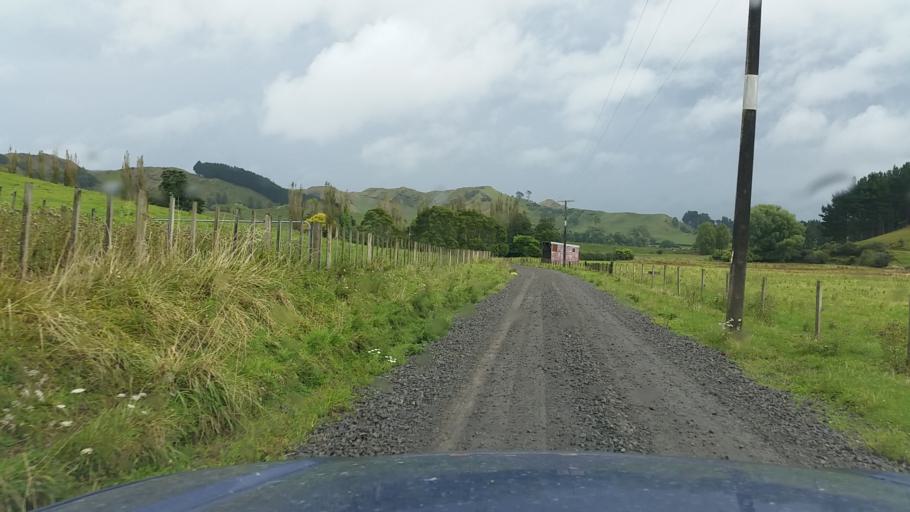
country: NZ
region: Taranaki
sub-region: South Taranaki District
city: Eltham
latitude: -39.3440
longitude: 174.4737
